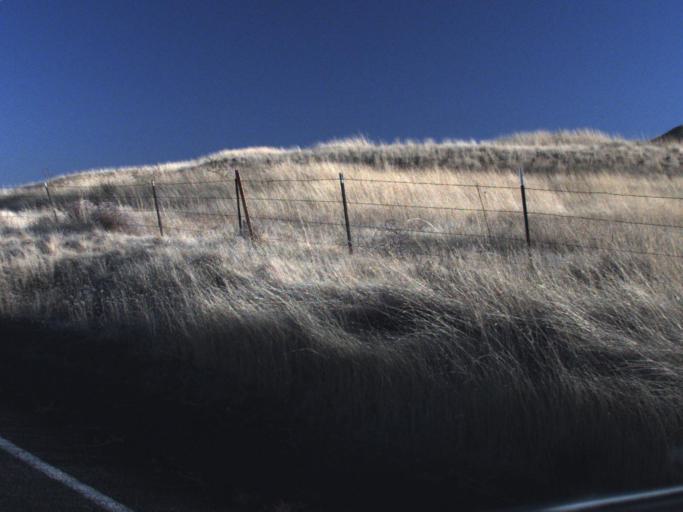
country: US
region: Washington
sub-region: Walla Walla County
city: Waitsburg
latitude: 46.6446
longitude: -118.2484
